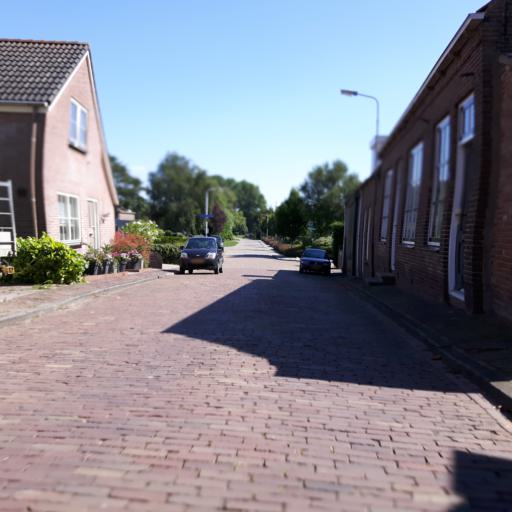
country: NL
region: Zeeland
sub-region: Schouwen-Duiveland
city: Bruinisse
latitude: 51.6260
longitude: 3.9842
